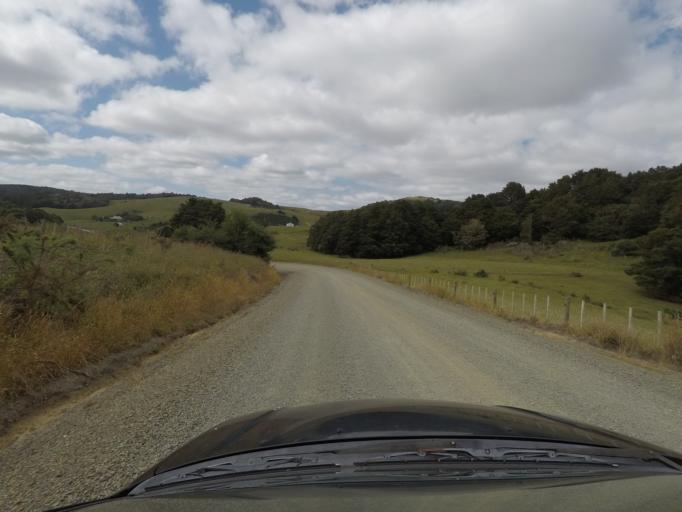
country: NZ
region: Northland
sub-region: Whangarei
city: Ruakaka
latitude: -35.9318
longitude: 174.3454
